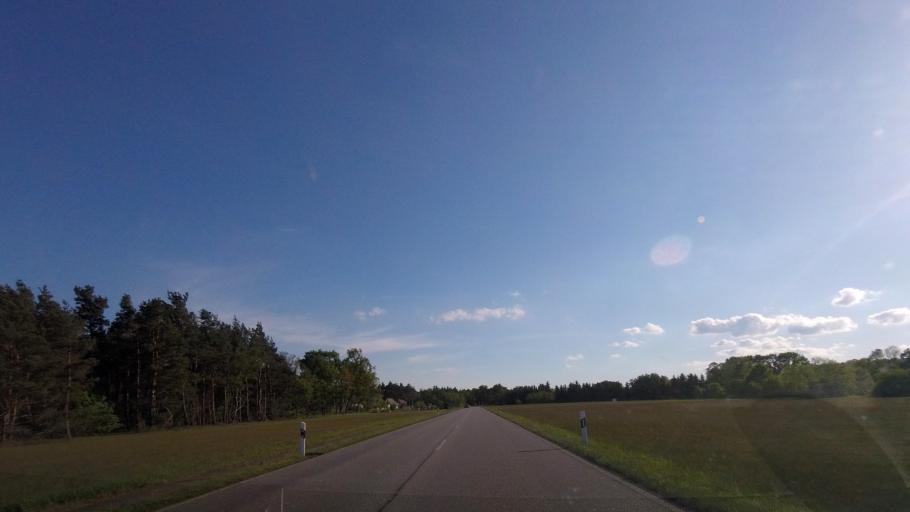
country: DE
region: Brandenburg
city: Luebben
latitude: 51.9122
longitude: 13.8656
